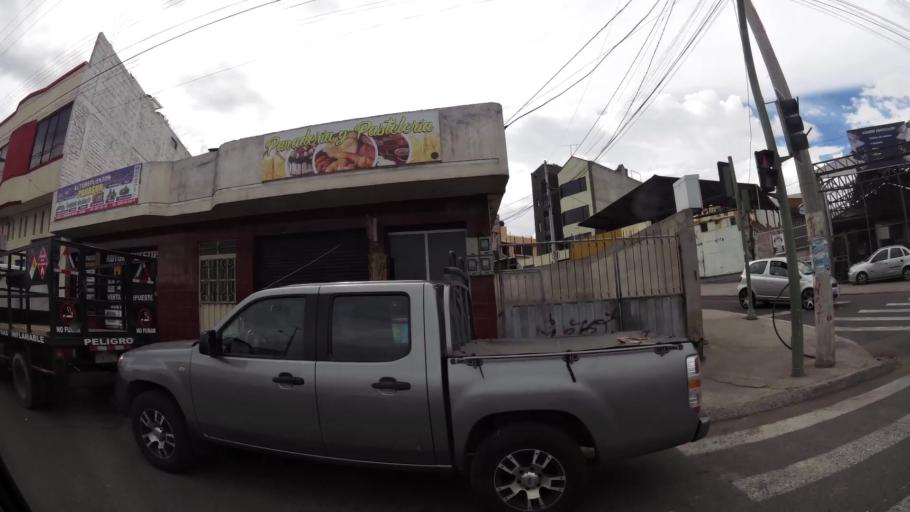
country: EC
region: Tungurahua
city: Ambato
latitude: -1.2791
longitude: -78.6307
